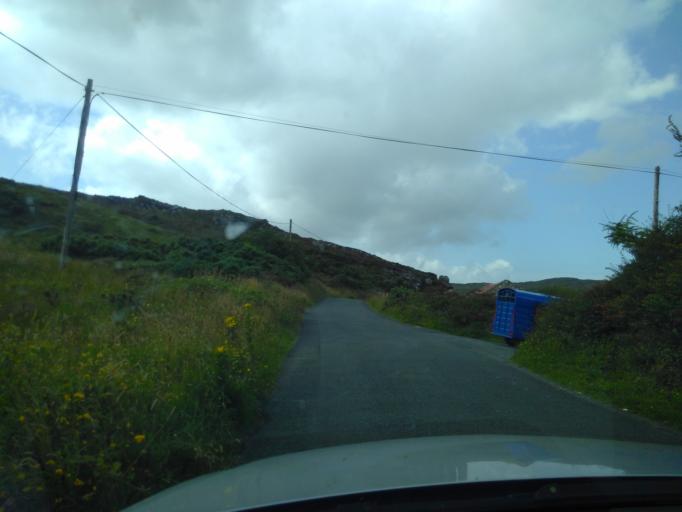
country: IE
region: Ulster
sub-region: County Donegal
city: Buncrana
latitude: 55.2230
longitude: -7.6161
